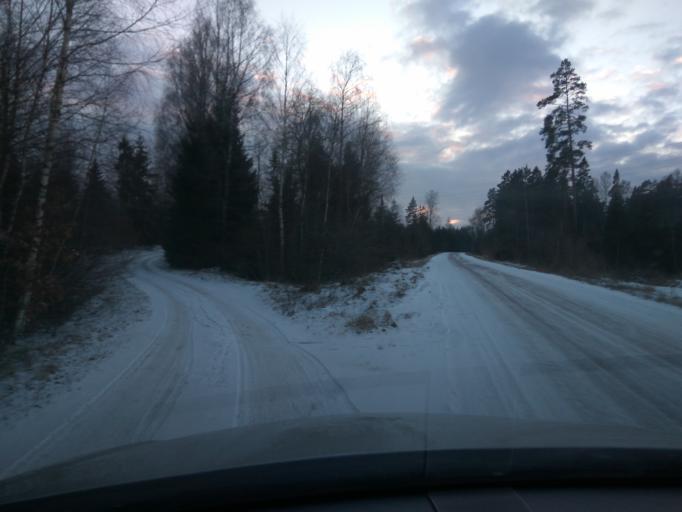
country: LV
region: Kuldigas Rajons
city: Kuldiga
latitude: 56.9151
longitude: 21.8949
